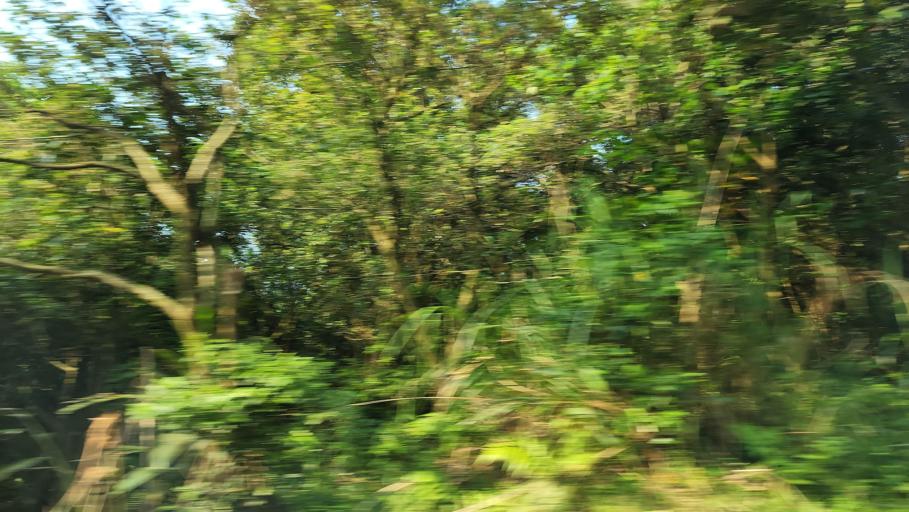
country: TW
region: Taiwan
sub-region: Keelung
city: Keelung
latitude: 25.1771
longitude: 121.6504
